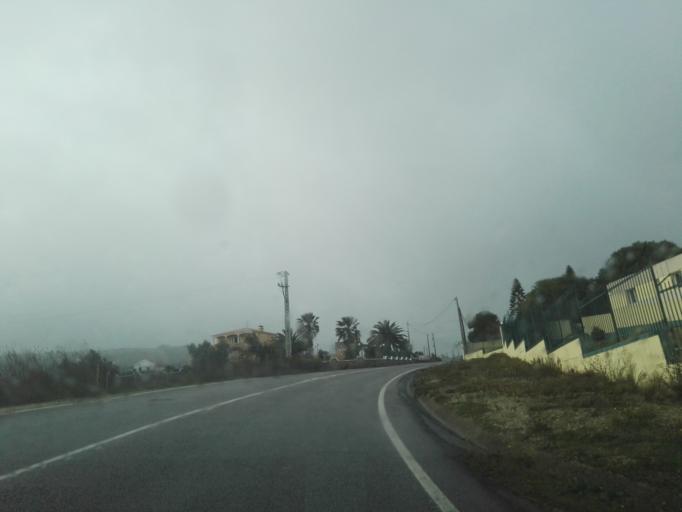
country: PT
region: Lisbon
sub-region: Vila Franca de Xira
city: Vialonga
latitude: 38.9029
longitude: -9.0579
